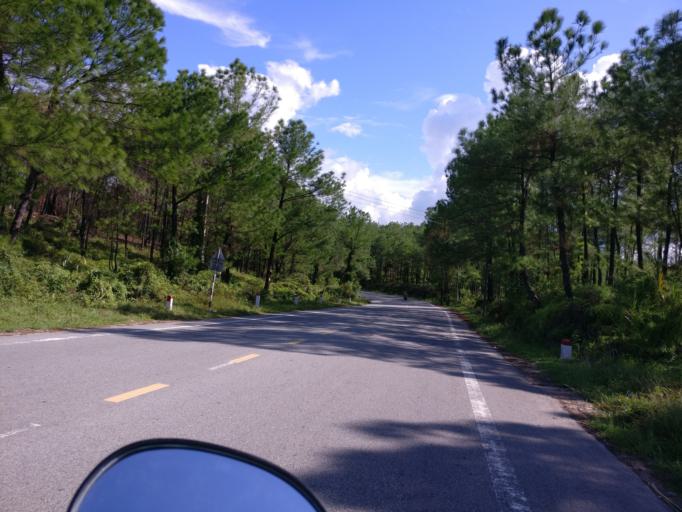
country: VN
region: Thua Thien-Hue
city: Hue
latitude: 16.4053
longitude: 107.5898
